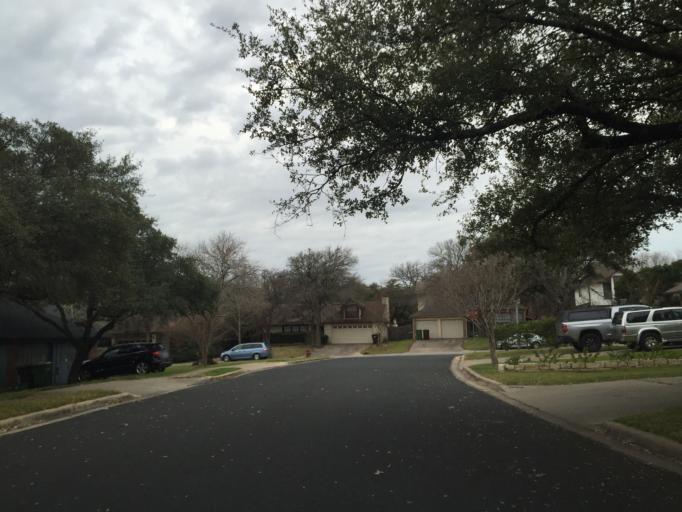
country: US
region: Texas
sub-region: Williamson County
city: Jollyville
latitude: 30.4482
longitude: -97.7480
